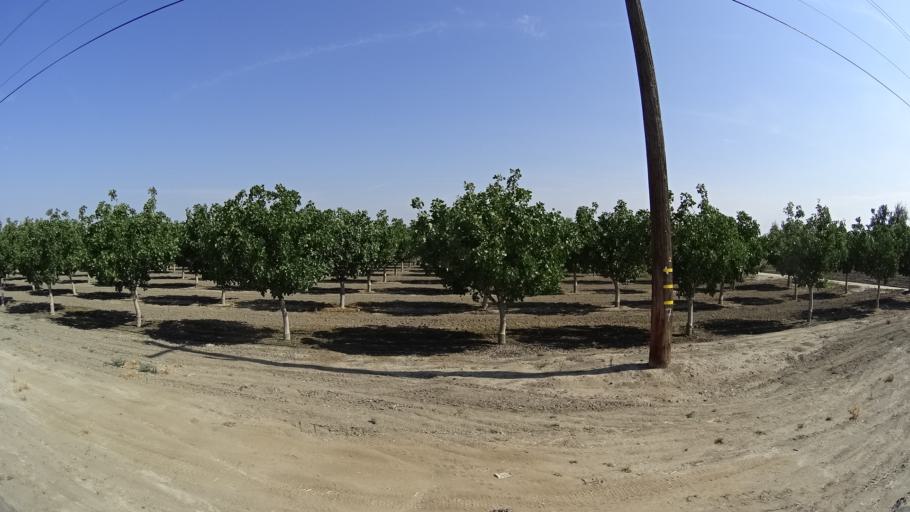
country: US
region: California
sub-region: Kings County
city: Lemoore
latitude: 36.3134
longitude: -119.8182
